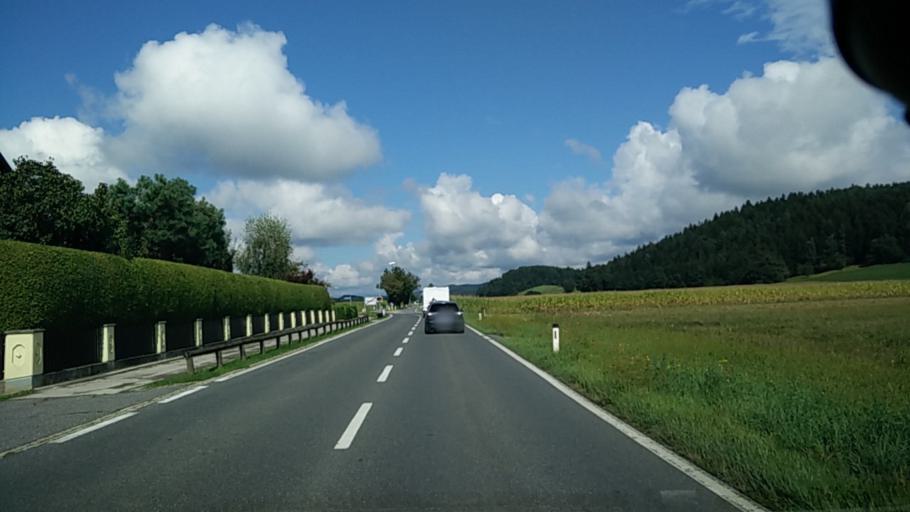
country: AT
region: Carinthia
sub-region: Politischer Bezirk Klagenfurt Land
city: Grafenstein
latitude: 46.6347
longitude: 14.5338
